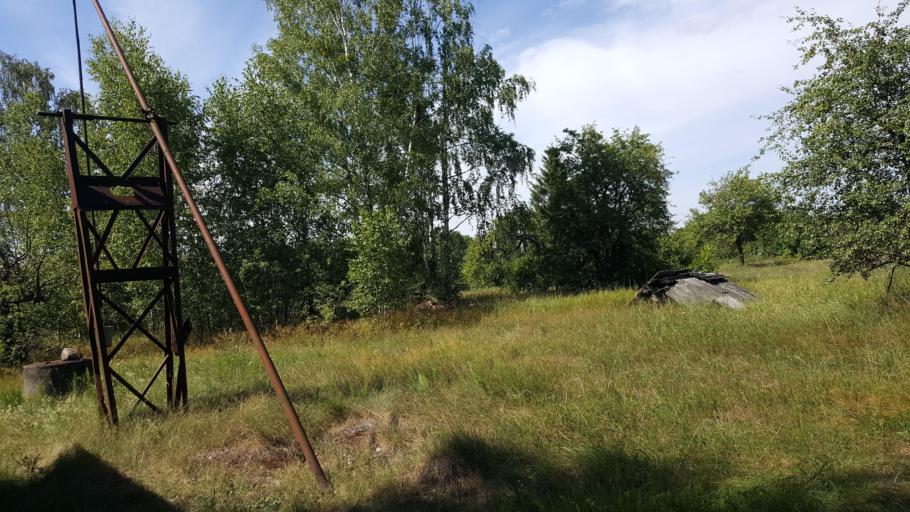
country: BY
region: Brest
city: Zhabinka
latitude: 52.4617
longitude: 24.1031
